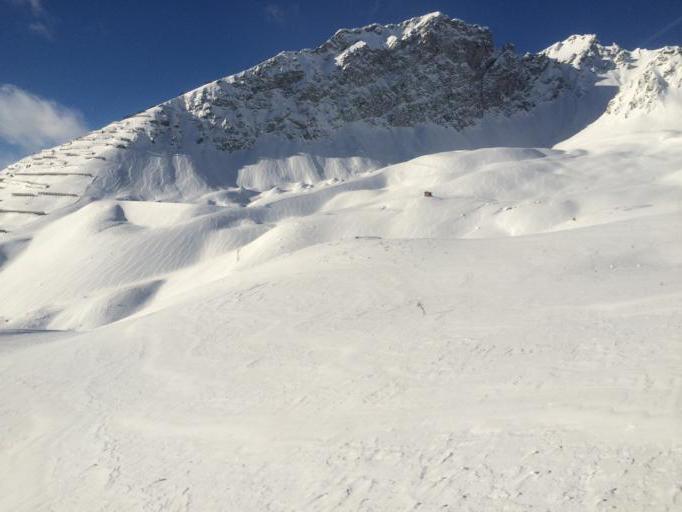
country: CH
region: Grisons
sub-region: Praettigau/Davos District
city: Davos
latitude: 46.8186
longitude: 9.8242
